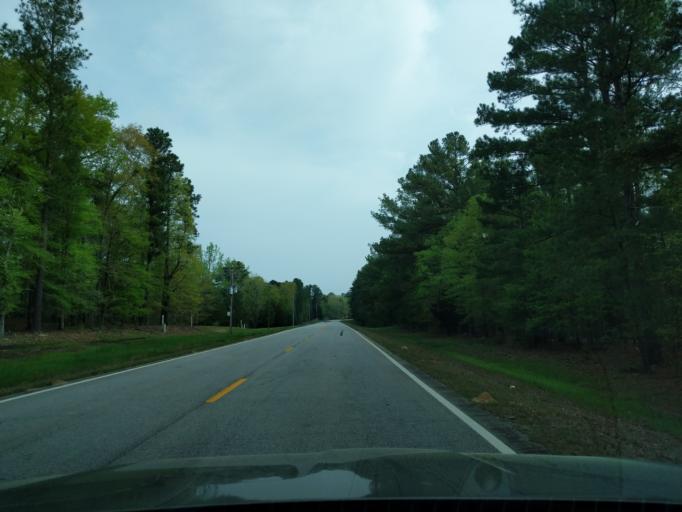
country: US
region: Georgia
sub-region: Lincoln County
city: Lincolnton
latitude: 33.8096
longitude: -82.4086
